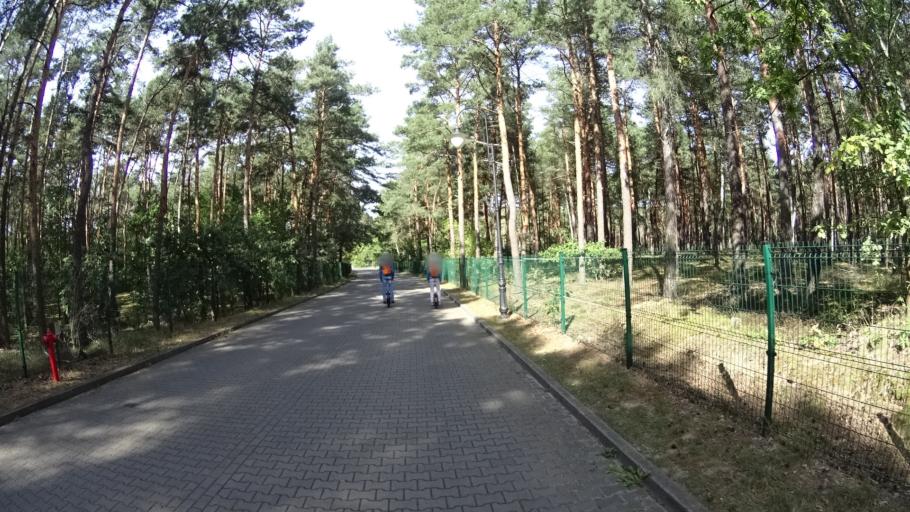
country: PL
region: Masovian Voivodeship
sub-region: Powiat legionowski
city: Bialobrzegi
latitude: 52.4601
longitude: 21.0740
